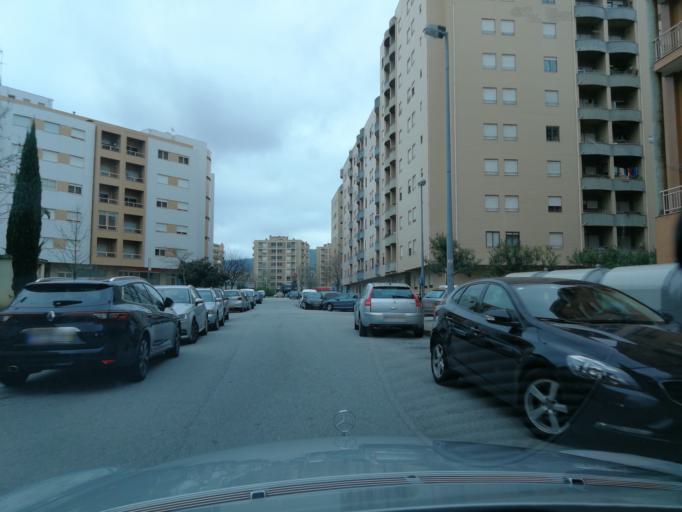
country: PT
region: Braga
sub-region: Braga
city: Braga
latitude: 41.5504
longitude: -8.4034
